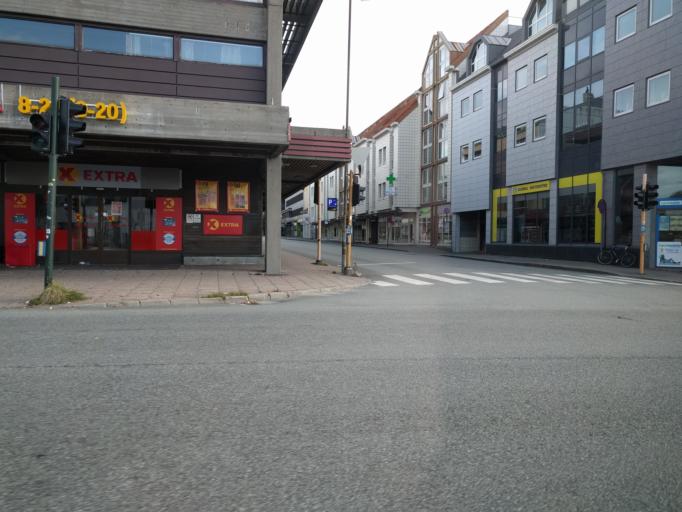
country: NO
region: Vest-Agder
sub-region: Kristiansand
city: Kristiansand
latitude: 58.1459
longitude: 7.9889
